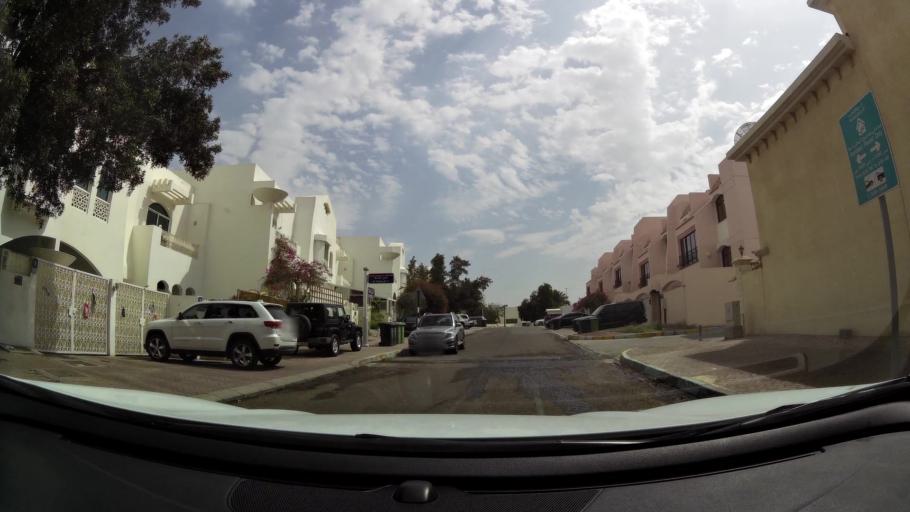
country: AE
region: Abu Dhabi
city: Abu Dhabi
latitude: 24.4654
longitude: 54.3394
